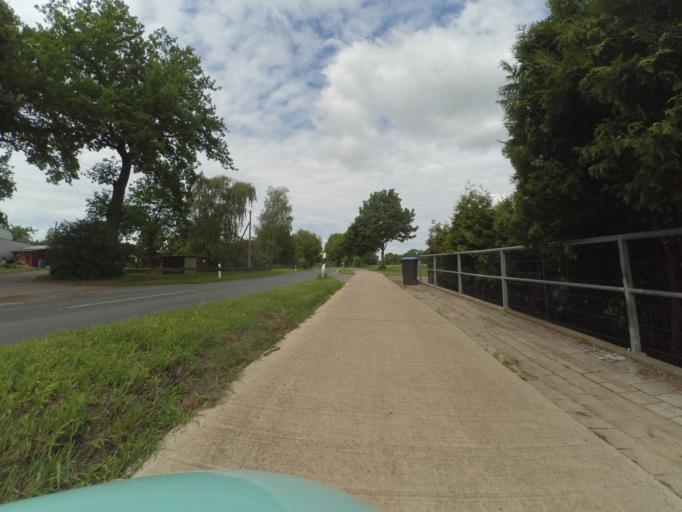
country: DE
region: Lower Saxony
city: Garbsen
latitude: 52.4277
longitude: 9.5257
